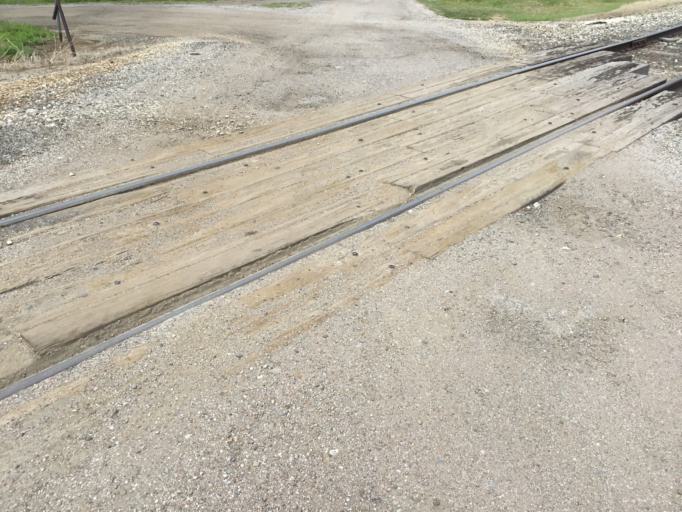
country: US
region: Kansas
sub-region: Butler County
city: El Dorado
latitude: 37.8309
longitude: -96.8428
